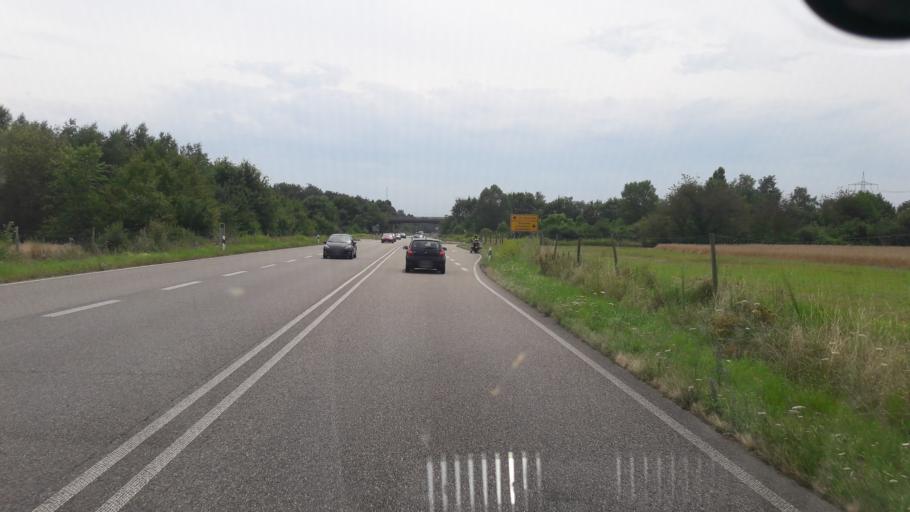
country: DE
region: Baden-Wuerttemberg
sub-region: Karlsruhe Region
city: Linkenheim-Hochstetten
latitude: 49.1205
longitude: 8.4301
